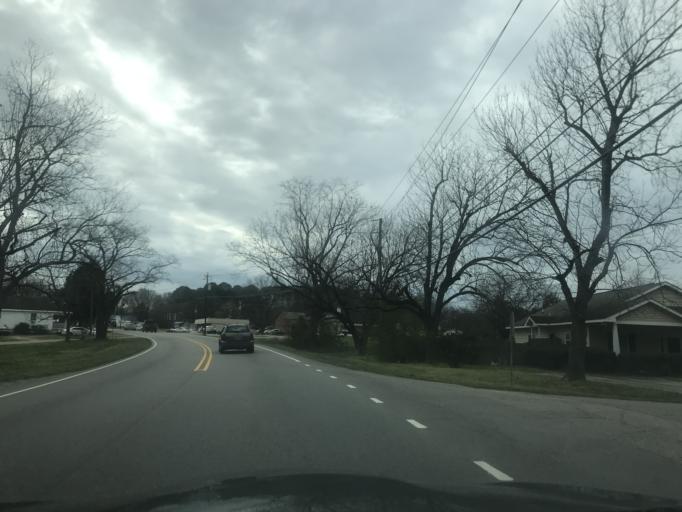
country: US
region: North Carolina
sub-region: Franklin County
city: Franklinton
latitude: 36.1042
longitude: -78.4466
